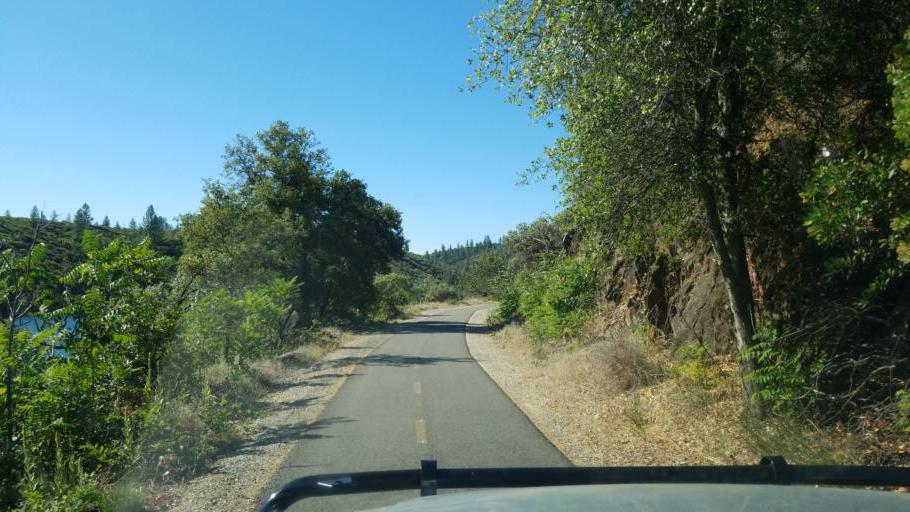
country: US
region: California
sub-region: Shasta County
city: Shasta
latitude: 40.6679
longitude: -122.4606
